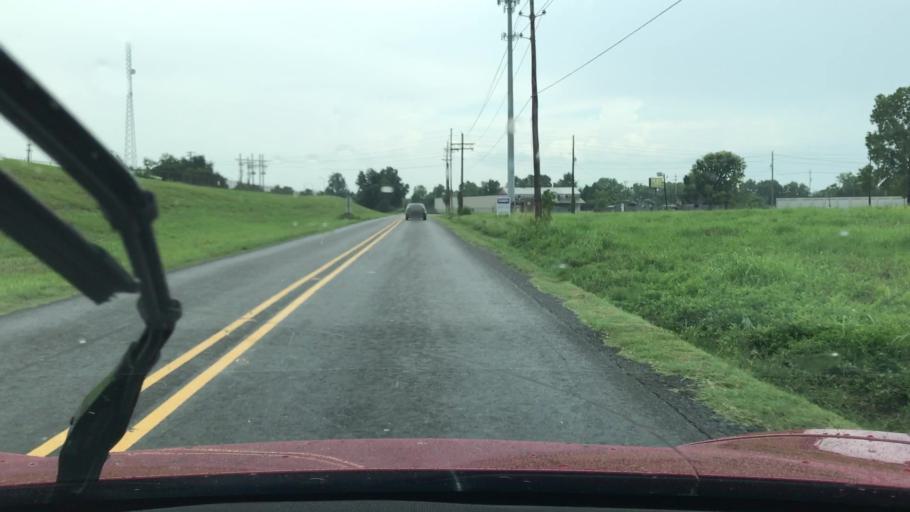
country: US
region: Louisiana
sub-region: Bossier Parish
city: Bossier City
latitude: 32.4026
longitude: -93.6910
